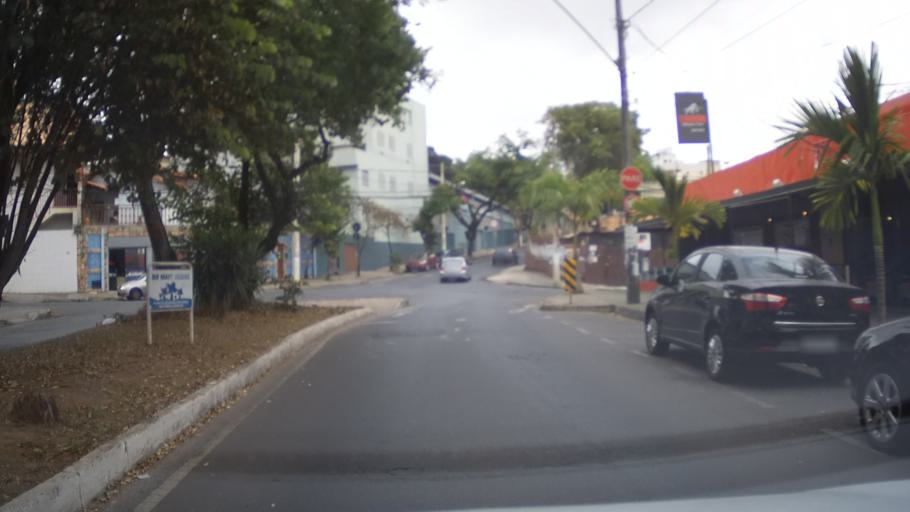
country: BR
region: Minas Gerais
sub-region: Belo Horizonte
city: Belo Horizonte
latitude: -19.8602
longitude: -43.9470
